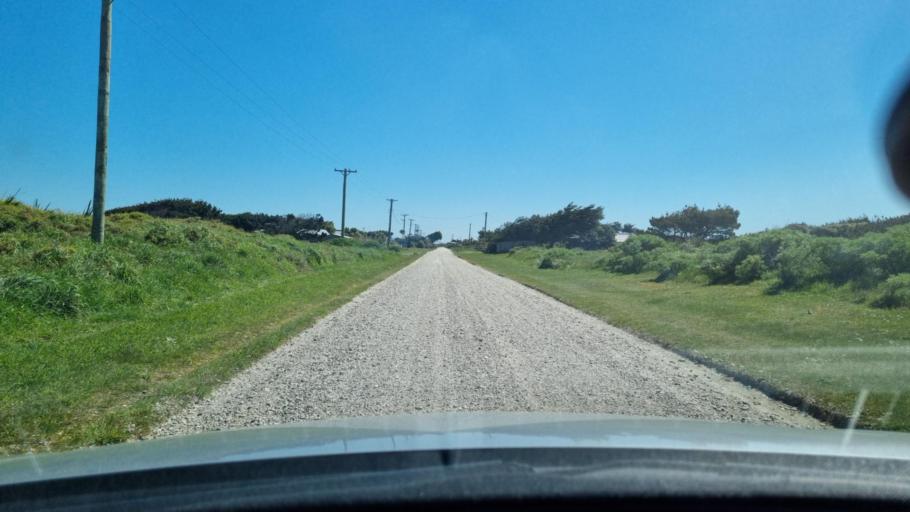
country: NZ
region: Southland
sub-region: Invercargill City
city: Invercargill
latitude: -46.4324
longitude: 168.2350
